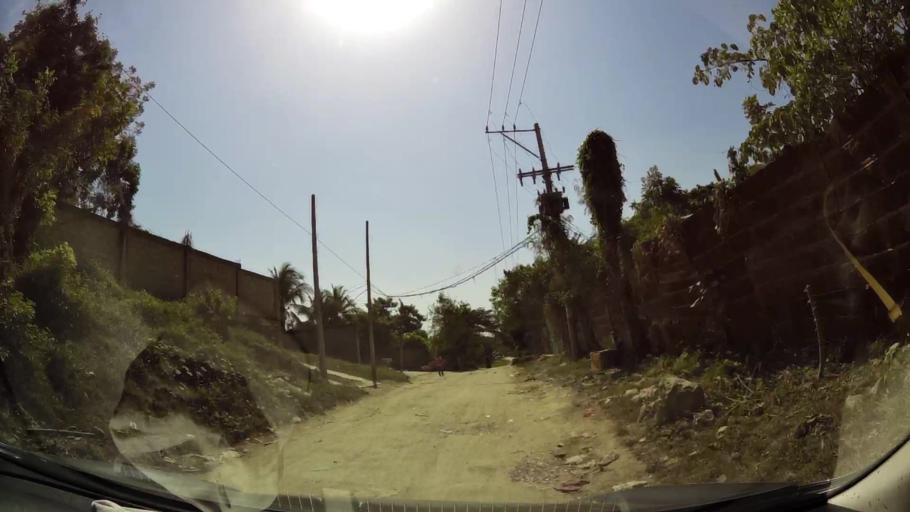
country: CO
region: Bolivar
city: Cartagena
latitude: 10.3704
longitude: -75.4943
